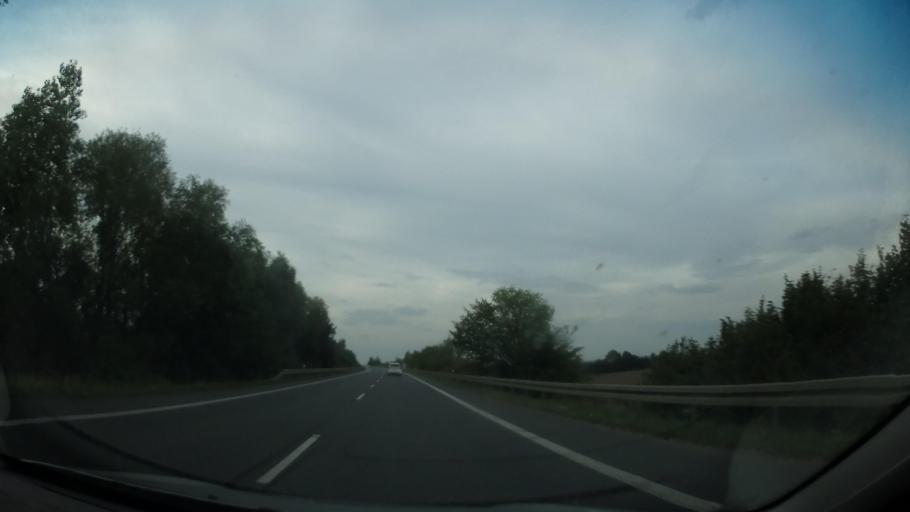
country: CZ
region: Central Bohemia
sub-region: Okres Kutna Hora
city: Caslav
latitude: 49.9087
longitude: 15.4066
